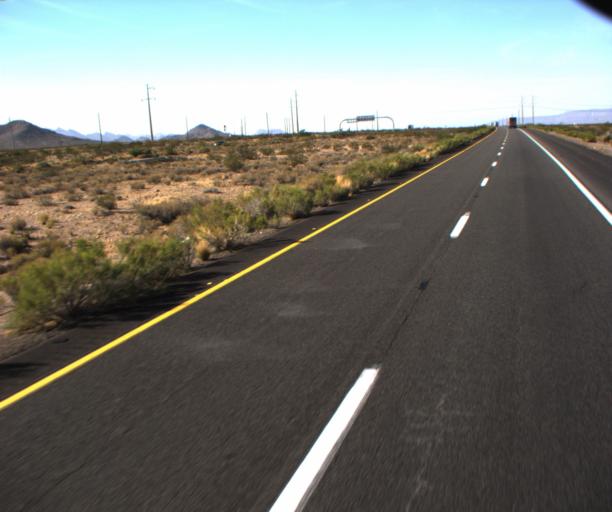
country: US
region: Arizona
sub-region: Mohave County
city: Kingman
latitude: 35.1114
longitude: -114.1159
